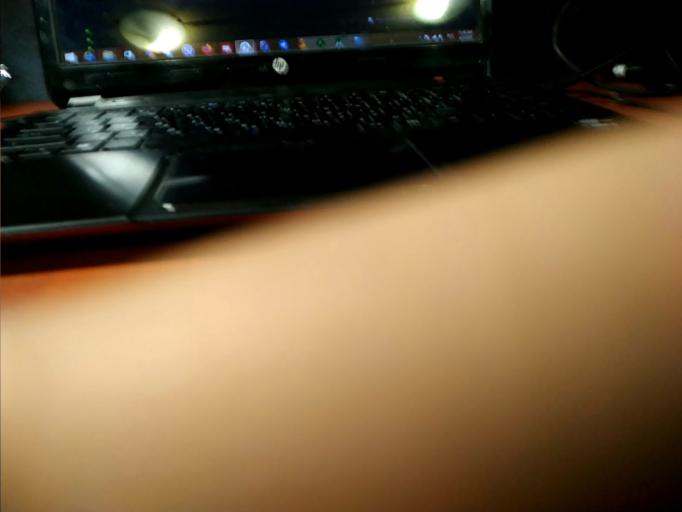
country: RU
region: Tverskaya
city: Sakharovo
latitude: 57.1020
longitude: 36.1200
